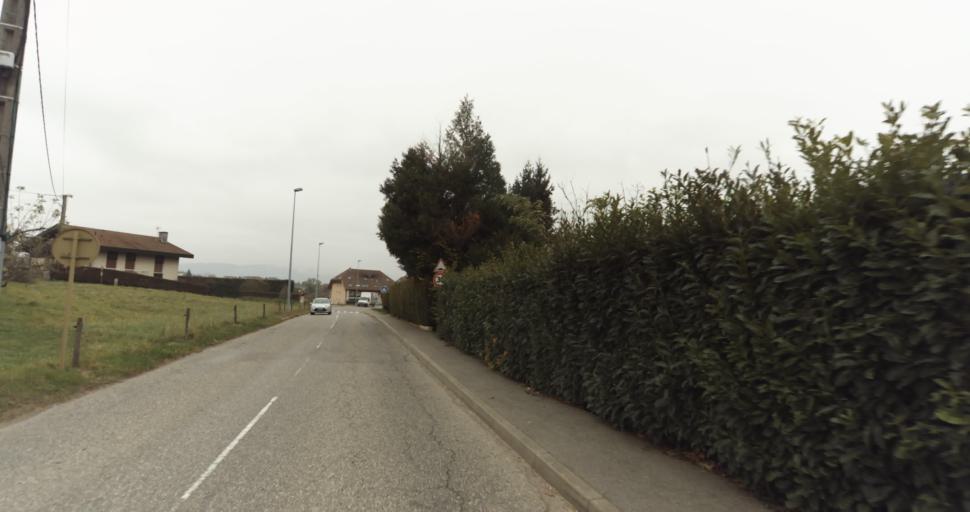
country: FR
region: Rhone-Alpes
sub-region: Departement de la Haute-Savoie
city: Poisy
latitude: 45.9325
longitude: 6.0624
